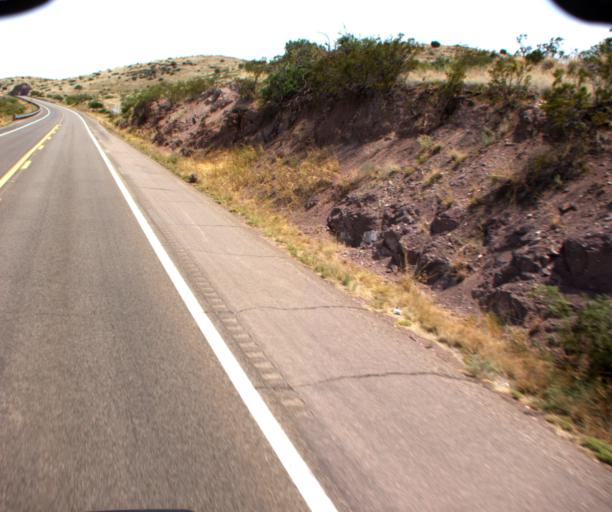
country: US
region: Arizona
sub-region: Greenlee County
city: Clifton
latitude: 32.7577
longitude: -109.2432
